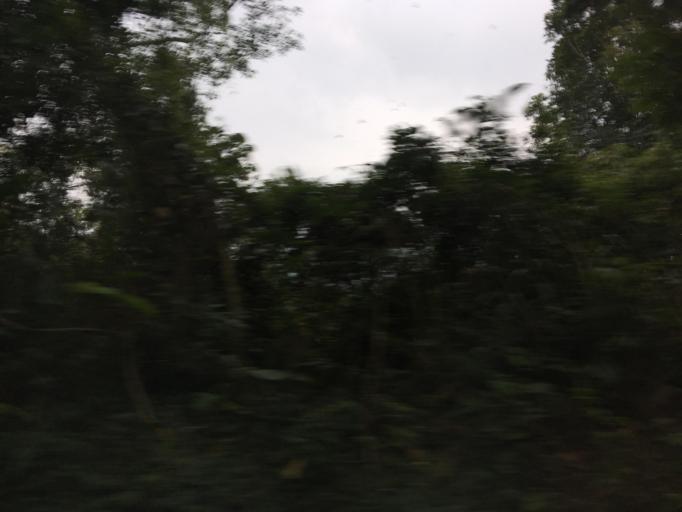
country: TW
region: Taiwan
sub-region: Yunlin
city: Douliu
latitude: 23.5461
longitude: 120.6189
